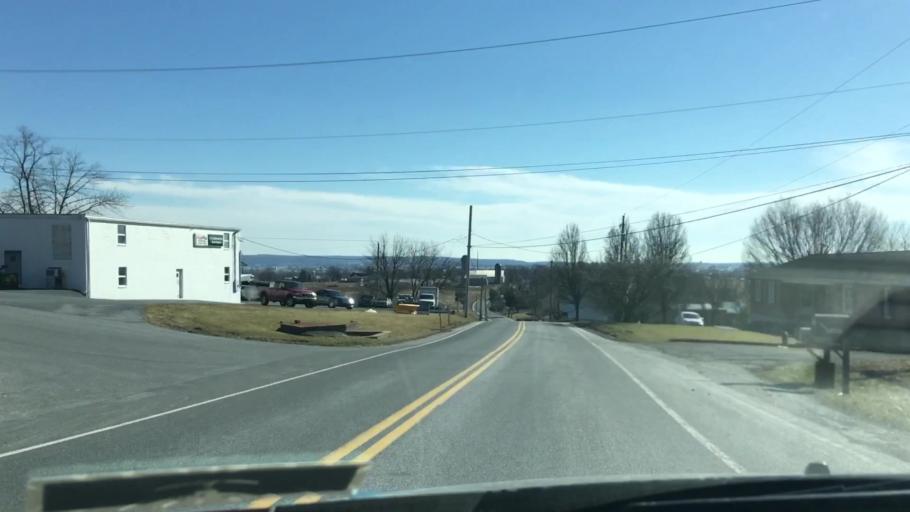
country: US
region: Pennsylvania
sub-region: Lancaster County
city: Reamstown
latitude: 40.1805
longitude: -76.1302
